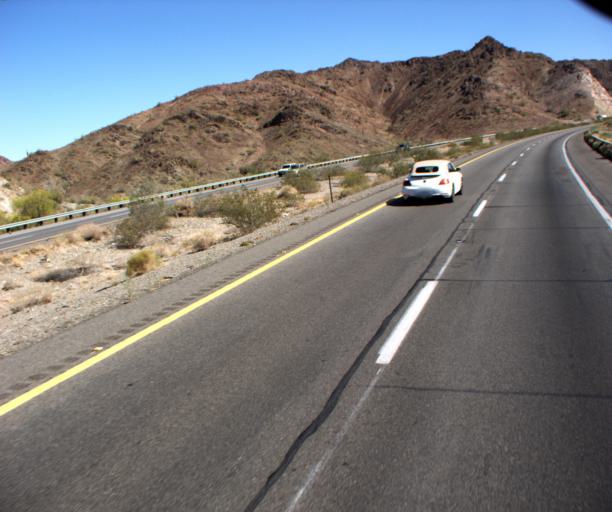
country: US
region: Arizona
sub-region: La Paz County
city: Ehrenberg
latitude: 33.6422
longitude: -114.3833
